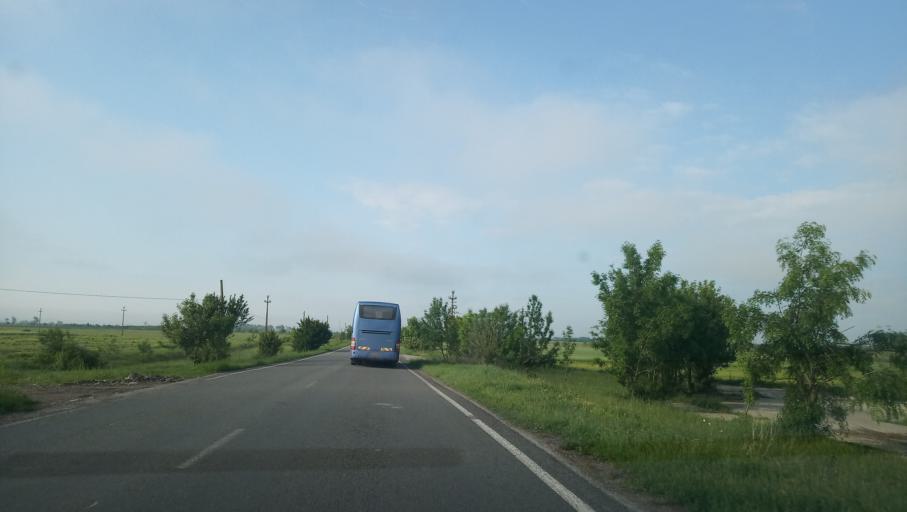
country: RO
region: Timis
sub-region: Comuna Moravita
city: Moravita
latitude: 45.2501
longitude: 21.2652
